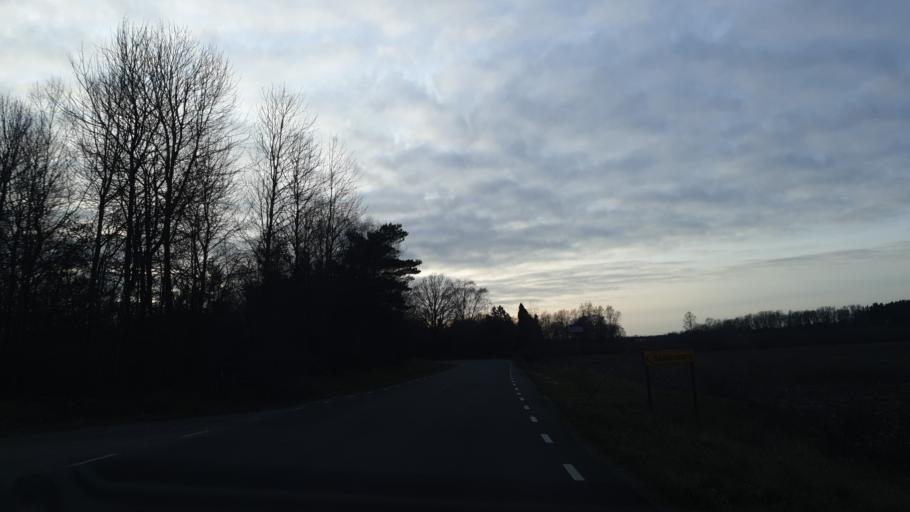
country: SE
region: Blekinge
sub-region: Karlskrona Kommun
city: Jaemjoe
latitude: 56.2247
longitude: 15.9901
